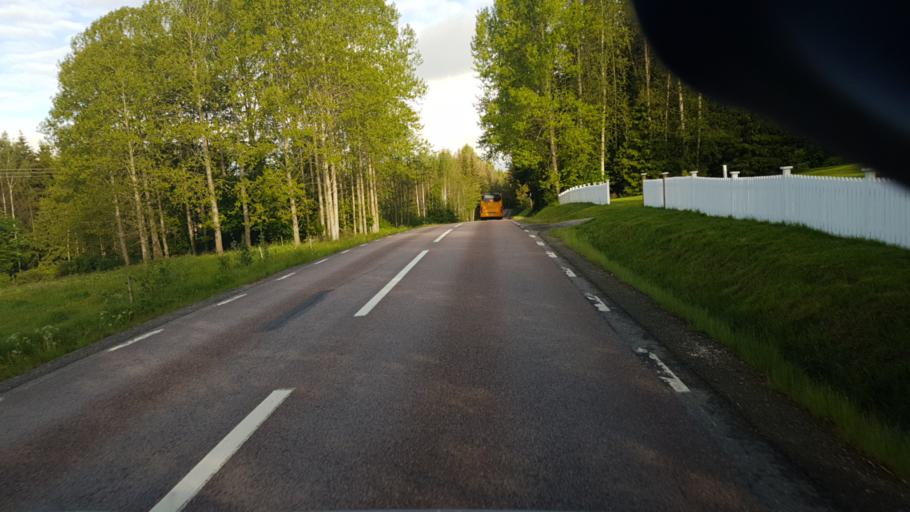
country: SE
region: Vaermland
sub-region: Eda Kommun
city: Amotfors
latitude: 59.7708
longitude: 12.3198
